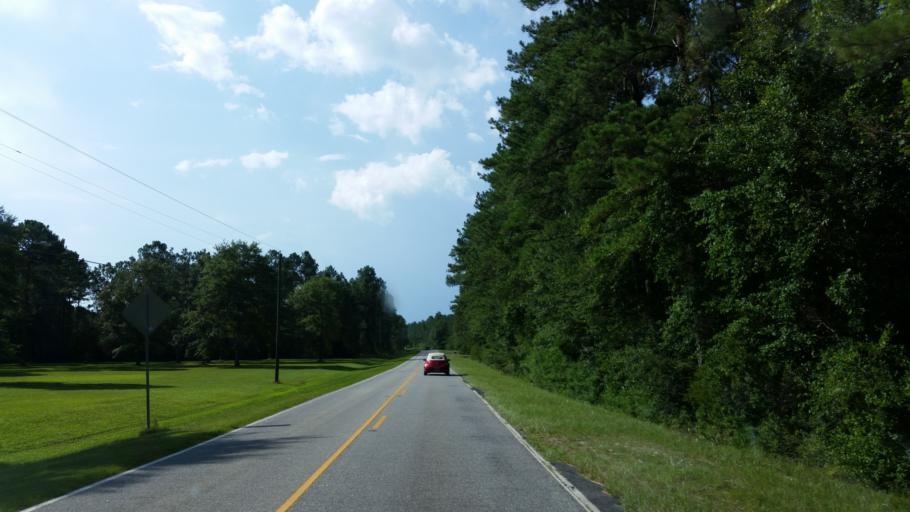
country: US
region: Georgia
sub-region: Lowndes County
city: Hahira
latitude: 30.9054
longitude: -83.3815
